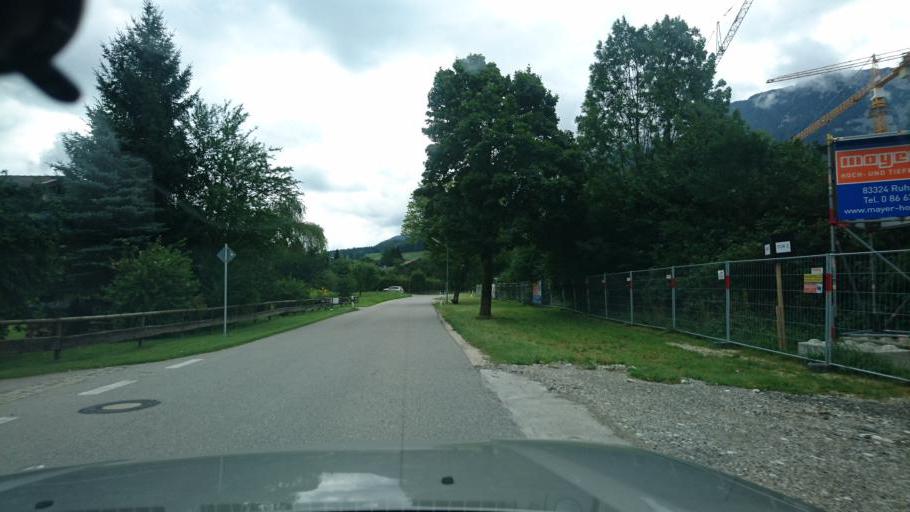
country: DE
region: Bavaria
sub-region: Upper Bavaria
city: Ruhpolding
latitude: 47.7560
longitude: 12.6648
